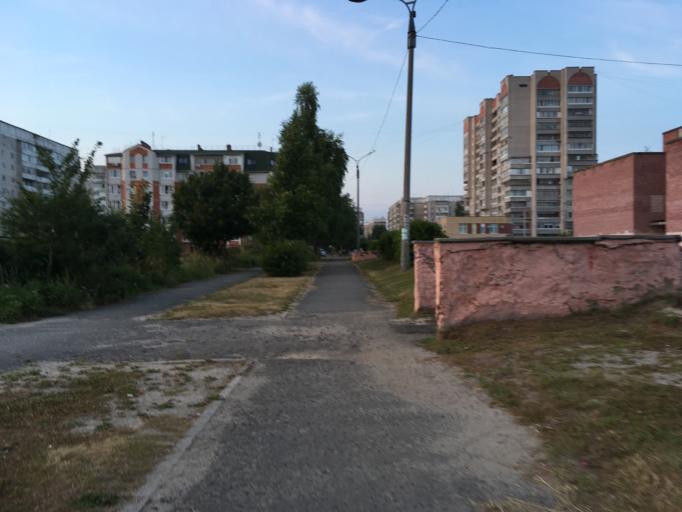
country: RU
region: Mariy-El
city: Yoshkar-Ola
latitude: 56.6275
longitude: 47.9209
